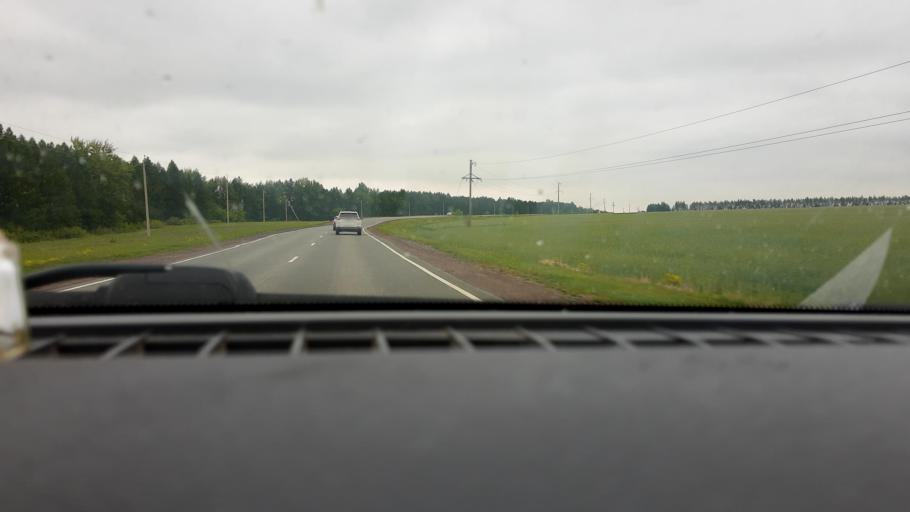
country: RU
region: Bashkortostan
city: Kandry
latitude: 54.4296
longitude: 53.9866
